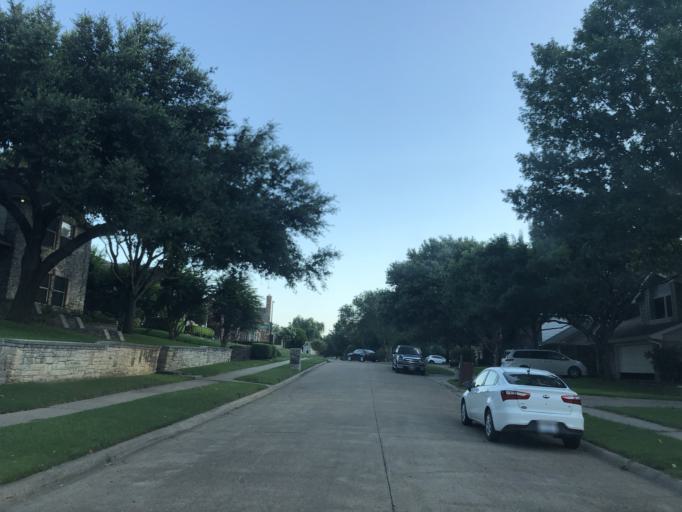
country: US
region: Texas
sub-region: Dallas County
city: Sunnyvale
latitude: 32.8429
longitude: -96.6073
